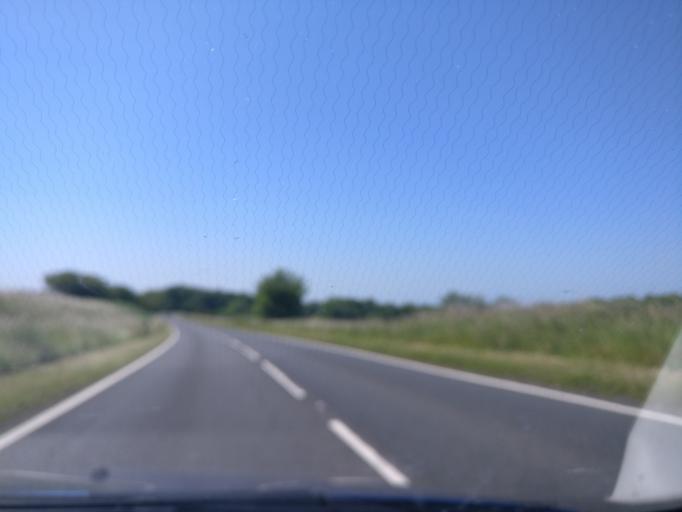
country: GB
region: Scotland
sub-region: East Lothian
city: Longniddry
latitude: 55.9838
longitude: -2.8655
